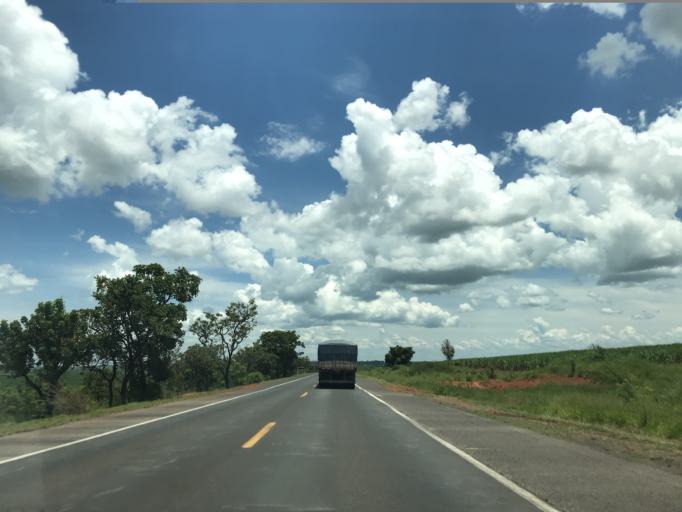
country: BR
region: Minas Gerais
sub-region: Prata
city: Prata
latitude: -19.5419
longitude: -48.8291
